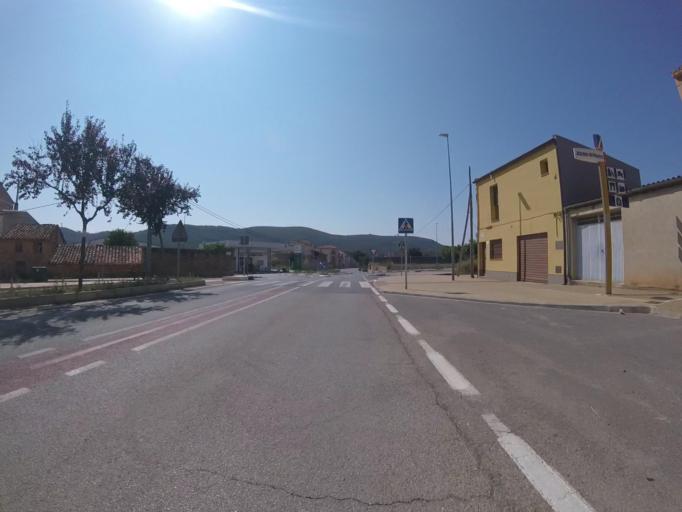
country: ES
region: Valencia
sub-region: Provincia de Castello
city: Adzaneta
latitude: 40.2199
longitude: -0.1710
